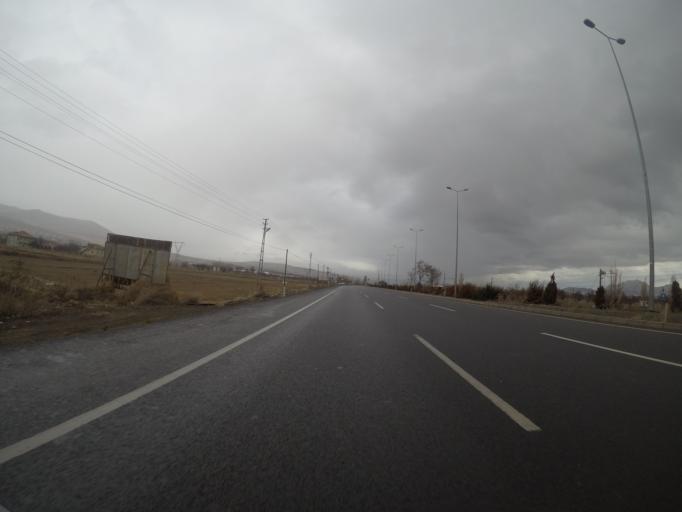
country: TR
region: Kayseri
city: Incesu
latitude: 38.6952
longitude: 35.2472
